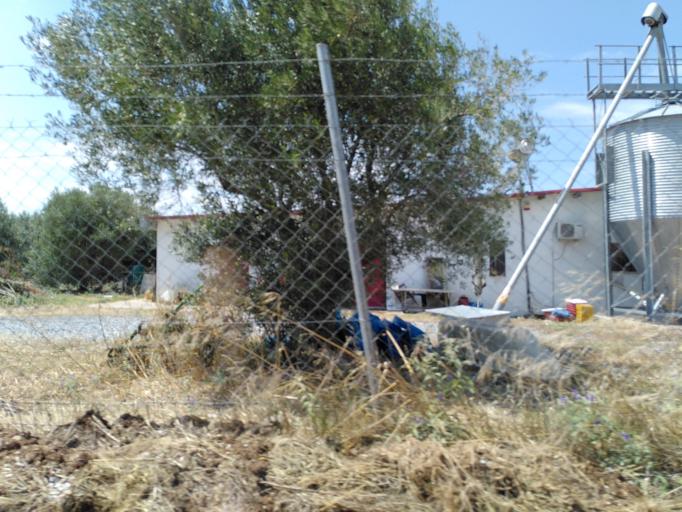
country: GR
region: Central Macedonia
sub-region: Nomos Thessalonikis
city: Agia Triada
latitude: 40.4981
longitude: 22.8472
